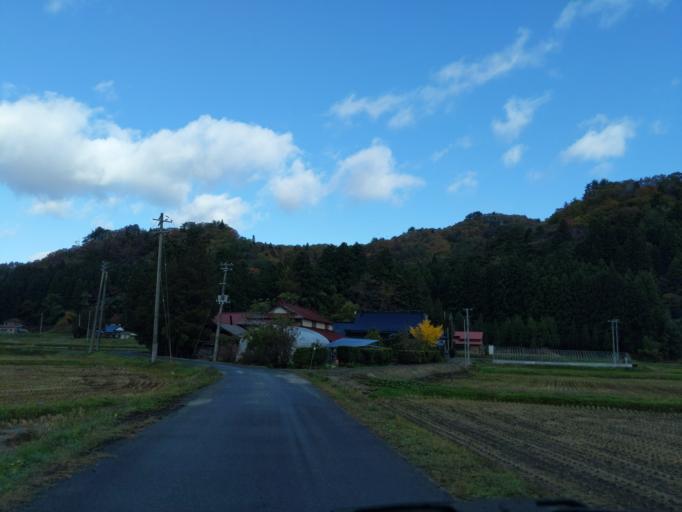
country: JP
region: Iwate
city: Ichinoseki
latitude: 38.9763
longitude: 140.9586
